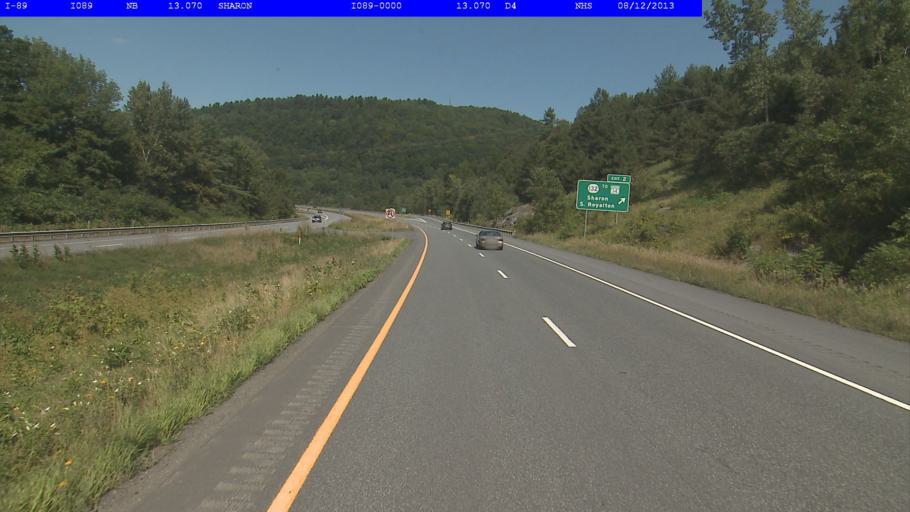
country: US
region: Vermont
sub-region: Windsor County
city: Woodstock
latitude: 43.7832
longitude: -72.4469
